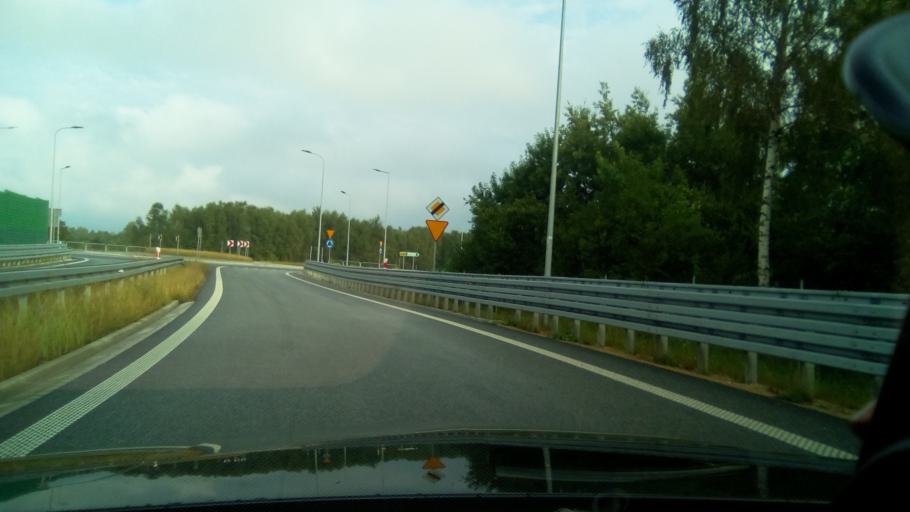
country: PL
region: Silesian Voivodeship
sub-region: Powiat czestochowski
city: Konopiska
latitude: 50.7490
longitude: 19.0484
